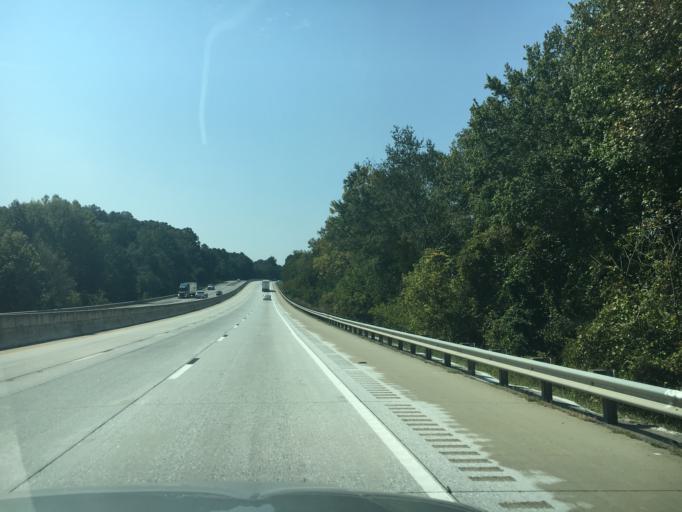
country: US
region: South Carolina
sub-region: Anderson County
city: Northlake
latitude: 34.6134
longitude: -82.6260
